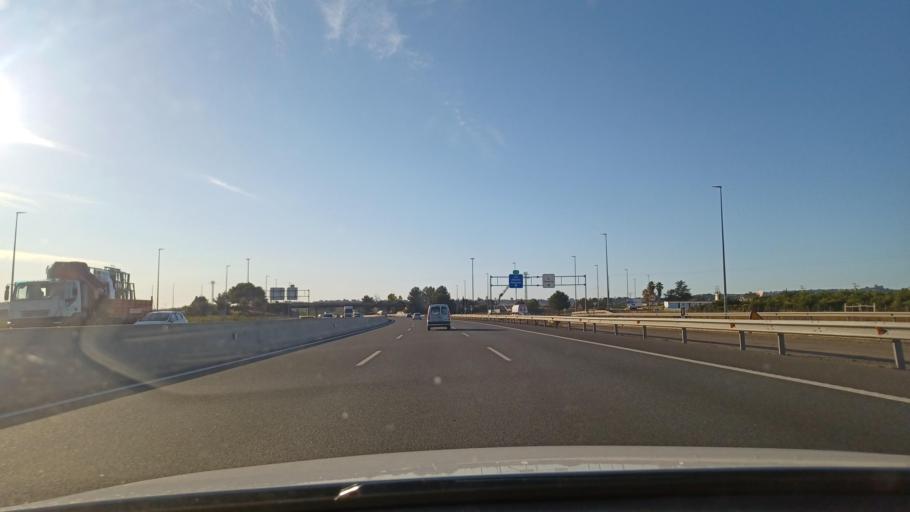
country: ES
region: Valencia
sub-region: Provincia de Valencia
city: Torrent
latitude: 39.4388
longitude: -0.5394
